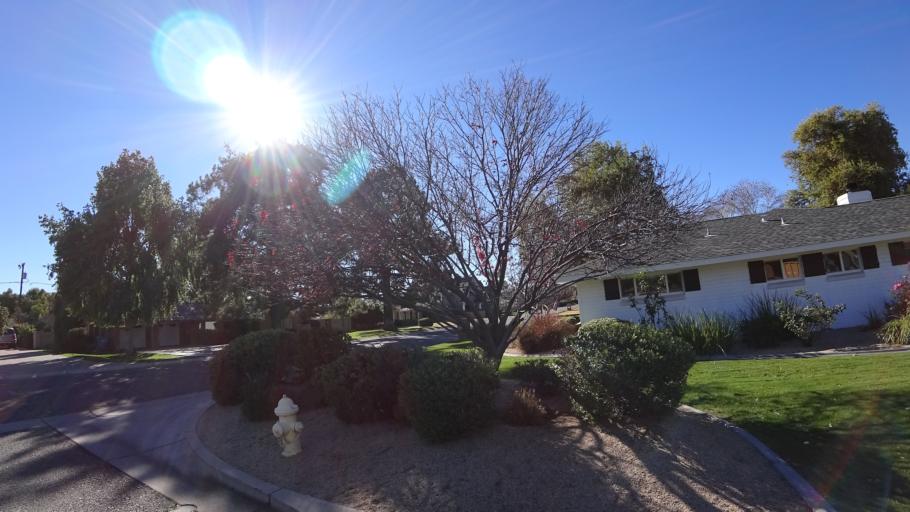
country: US
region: Arizona
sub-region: Maricopa County
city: Phoenix
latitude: 33.5421
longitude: -112.0715
